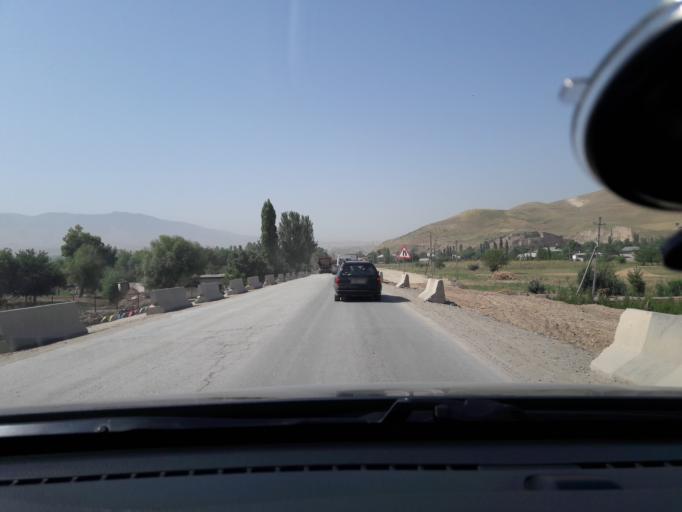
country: TJ
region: Dushanbe
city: Boshkengash
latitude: 38.4498
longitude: 68.7343
